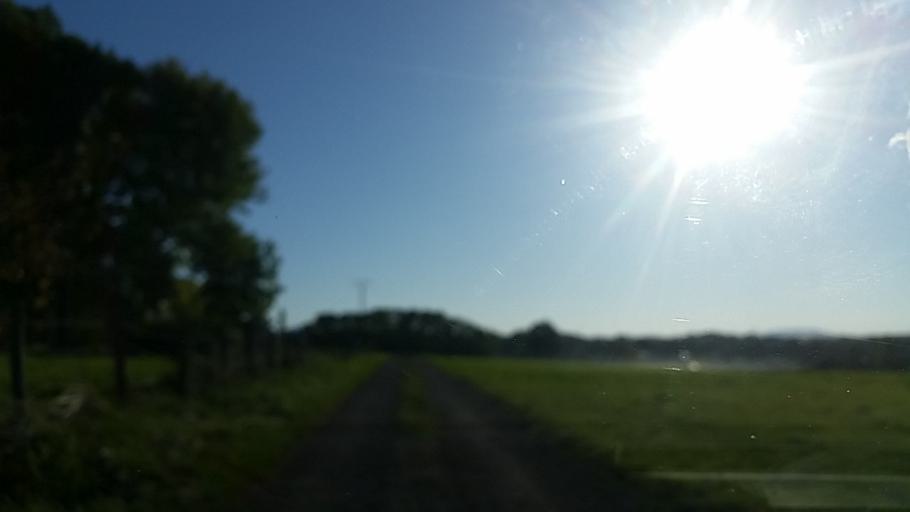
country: FR
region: Franche-Comte
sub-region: Departement du Doubs
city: Ornans
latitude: 47.0432
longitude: 6.0756
